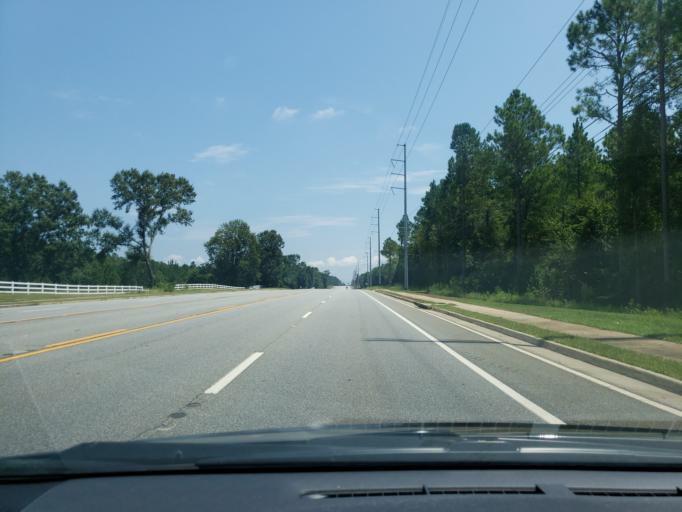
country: US
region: Georgia
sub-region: Dougherty County
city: Albany
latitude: 31.5856
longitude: -84.2613
